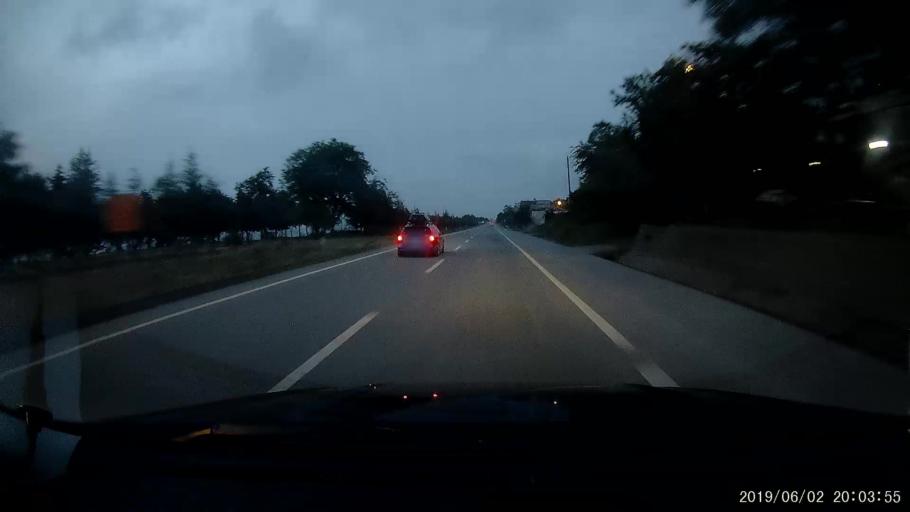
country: TR
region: Giresun
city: Tirebolu
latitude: 41.0267
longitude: 38.9014
